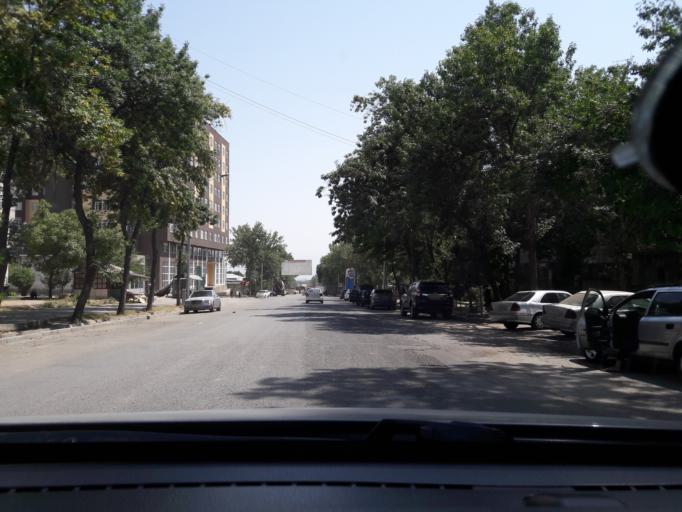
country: TJ
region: Dushanbe
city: Dushanbe
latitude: 38.5882
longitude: 68.7332
